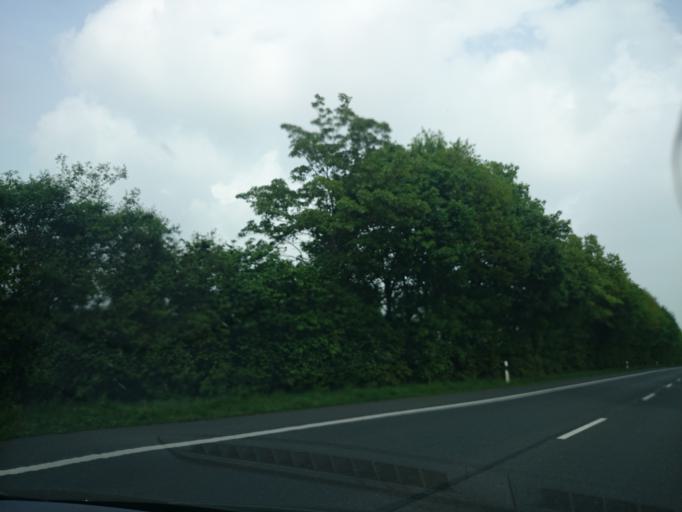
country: DE
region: North Rhine-Westphalia
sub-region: Regierungsbezirk Munster
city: Coesfeld
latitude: 51.9337
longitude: 7.1341
